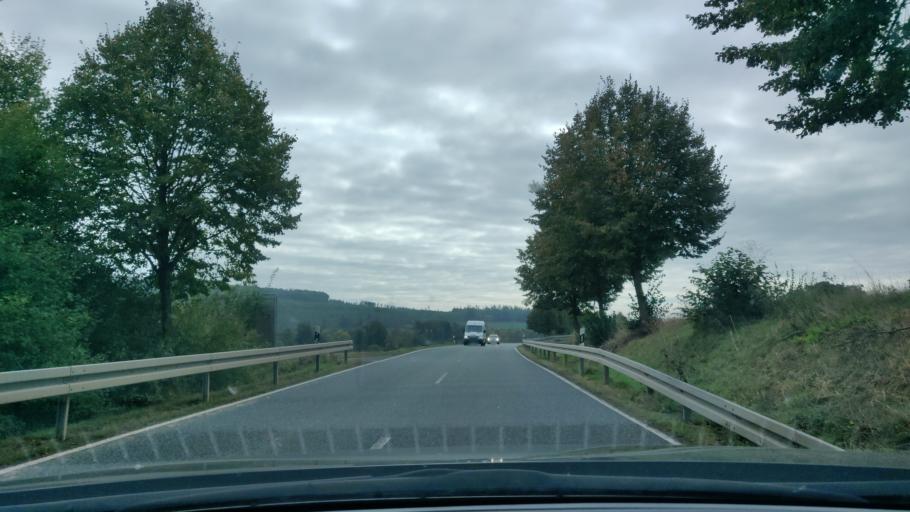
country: DE
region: Hesse
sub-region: Regierungsbezirk Kassel
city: Neuental
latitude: 50.9782
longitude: 9.2027
